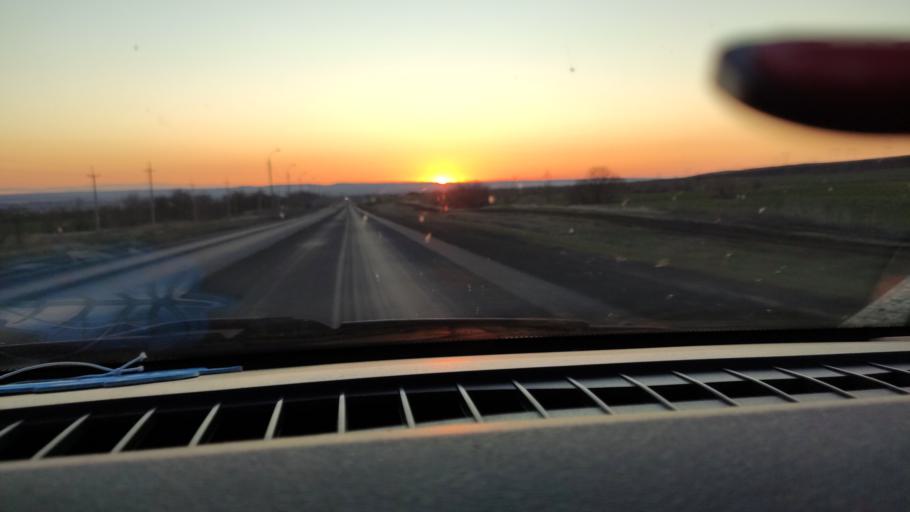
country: RU
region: Saratov
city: Shumeyka
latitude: 51.7875
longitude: 46.1423
